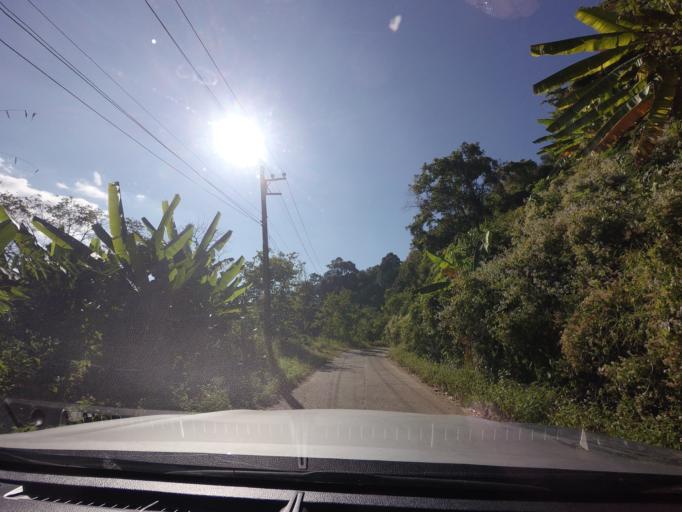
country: TH
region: Lampang
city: Mueang Pan
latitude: 18.8308
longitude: 99.3953
